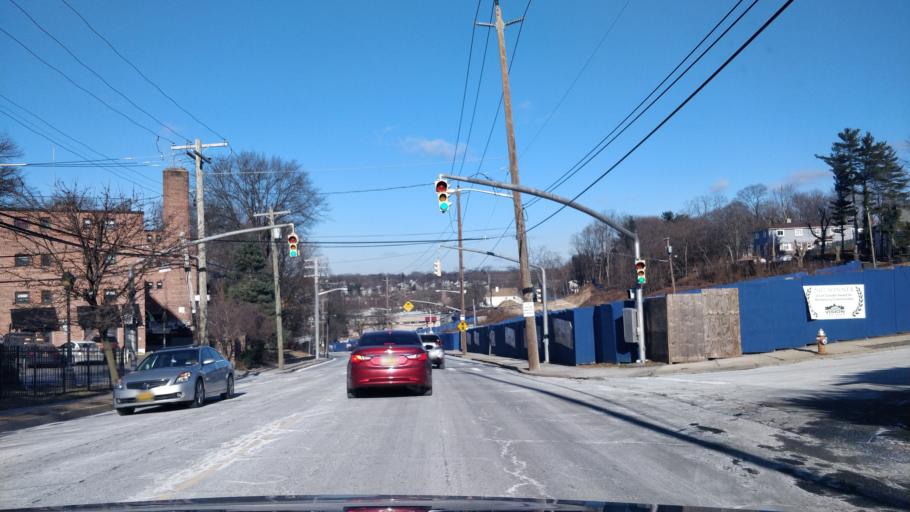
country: US
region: New York
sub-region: Nassau County
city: Glen Cove
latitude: 40.8546
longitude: -73.6344
